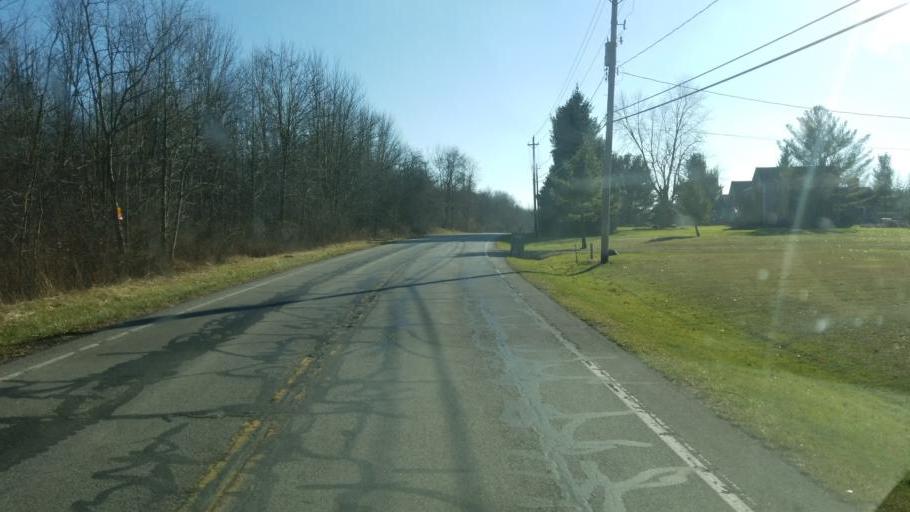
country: US
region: Ohio
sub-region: Geauga County
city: Bainbridge
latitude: 41.4032
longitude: -81.2466
